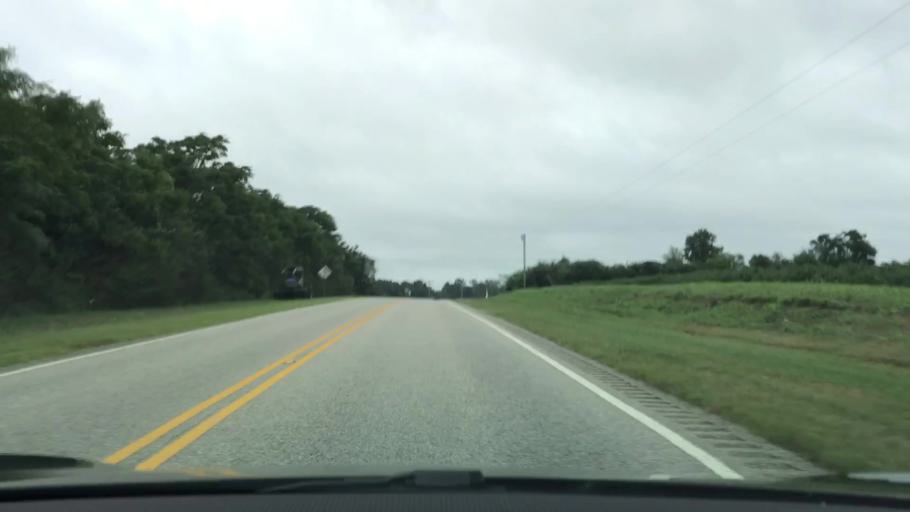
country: US
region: Alabama
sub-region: Coffee County
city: Elba
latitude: 31.3368
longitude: -86.1314
